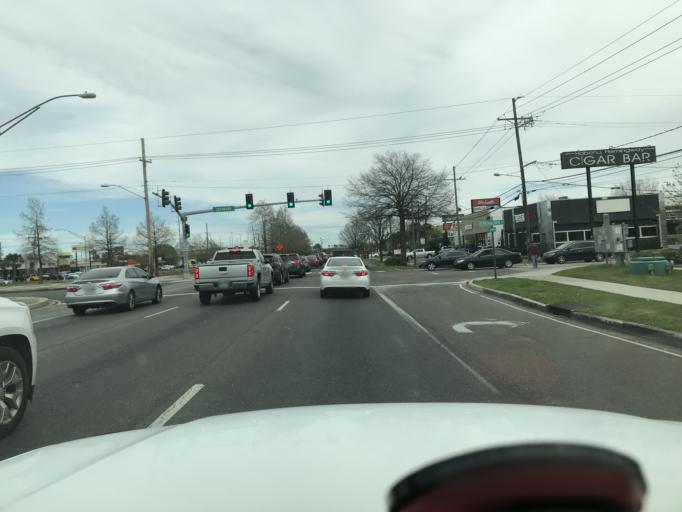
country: US
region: Louisiana
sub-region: Jefferson Parish
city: Metairie
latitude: 30.0034
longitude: -90.1626
